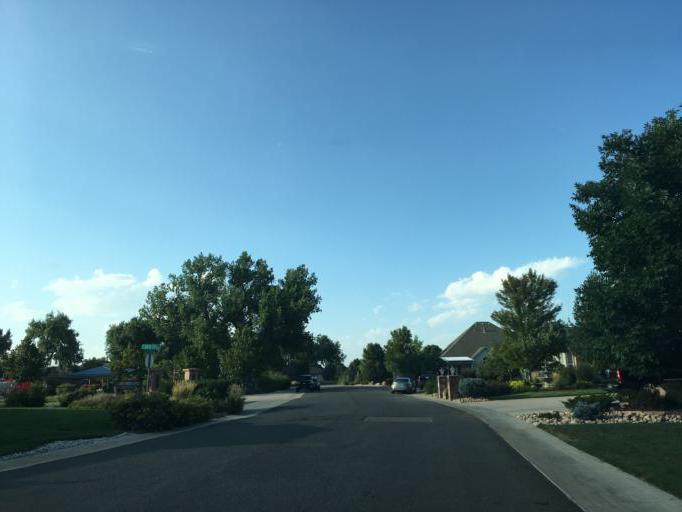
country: US
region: Colorado
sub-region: Jefferson County
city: Applewood
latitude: 39.7935
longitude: -105.1693
